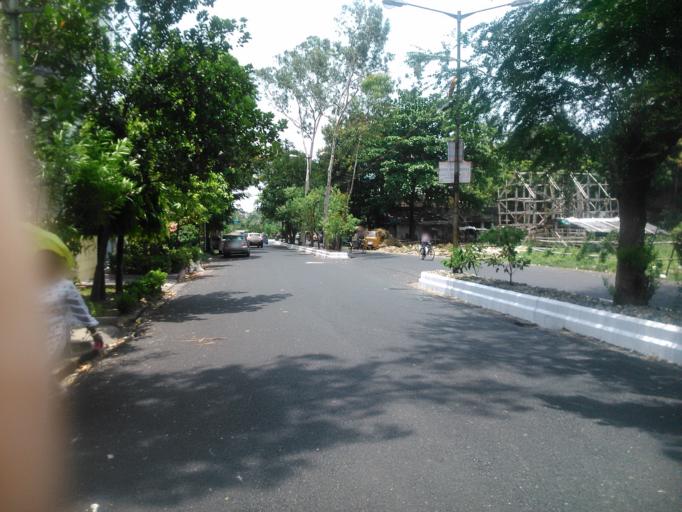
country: IN
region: West Bengal
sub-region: North 24 Parganas
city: Garui
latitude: 22.5961
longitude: 88.4101
